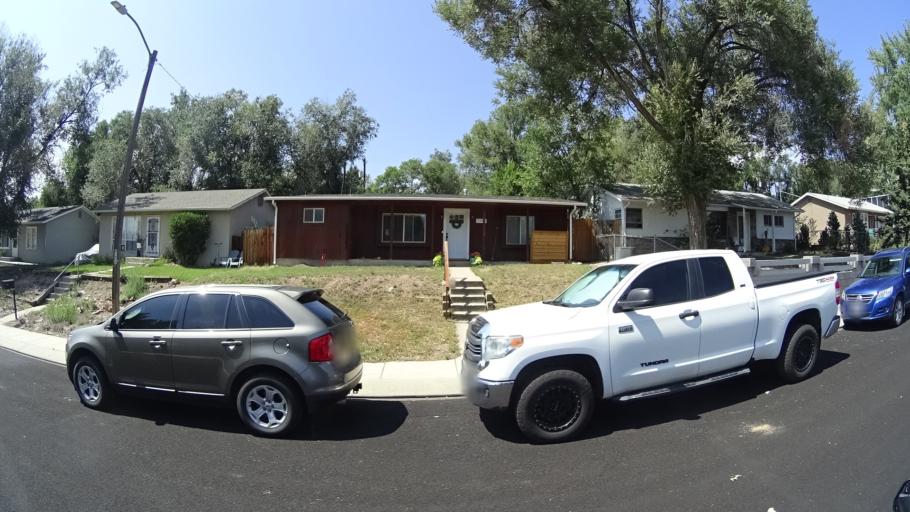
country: US
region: Colorado
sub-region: El Paso County
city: Colorado Springs
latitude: 38.8743
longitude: -104.8371
